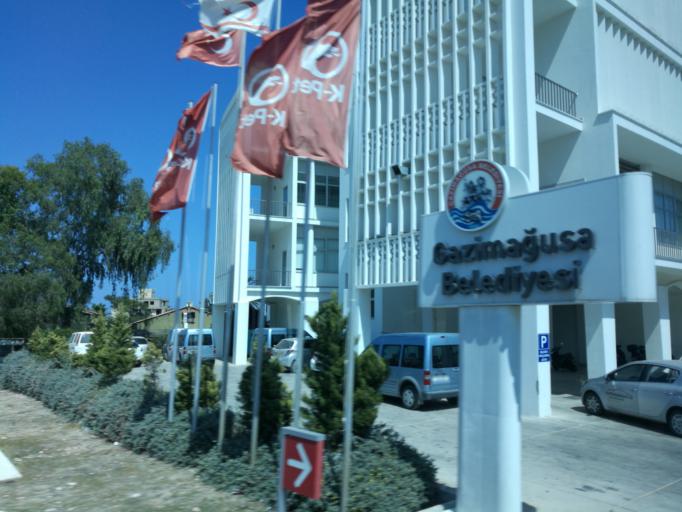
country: CY
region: Ammochostos
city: Famagusta
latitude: 35.1159
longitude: 33.9449
